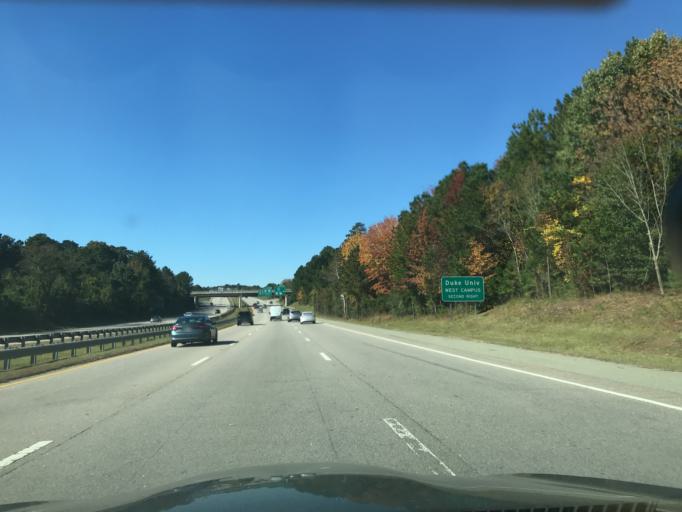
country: US
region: North Carolina
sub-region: Durham County
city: Durham
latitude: 36.0156
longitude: -78.9425
